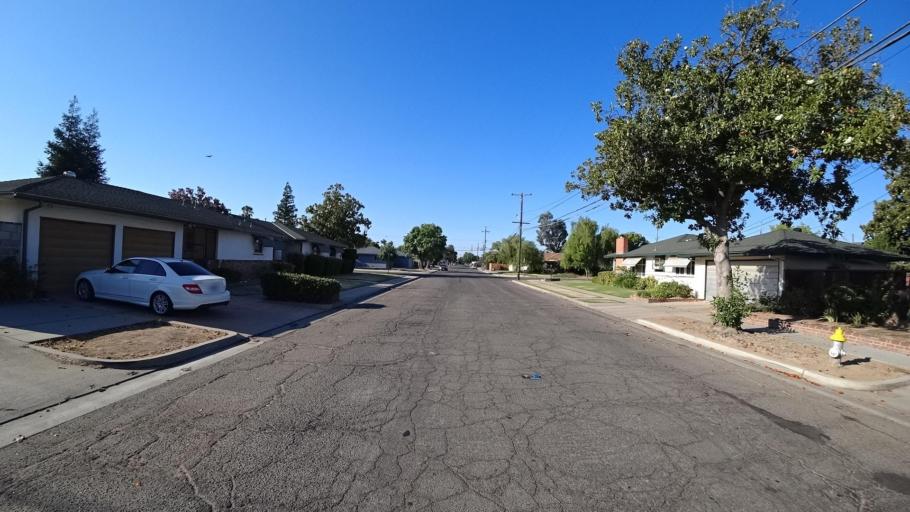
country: US
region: California
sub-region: Fresno County
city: Fresno
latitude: 36.7706
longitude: -119.8289
